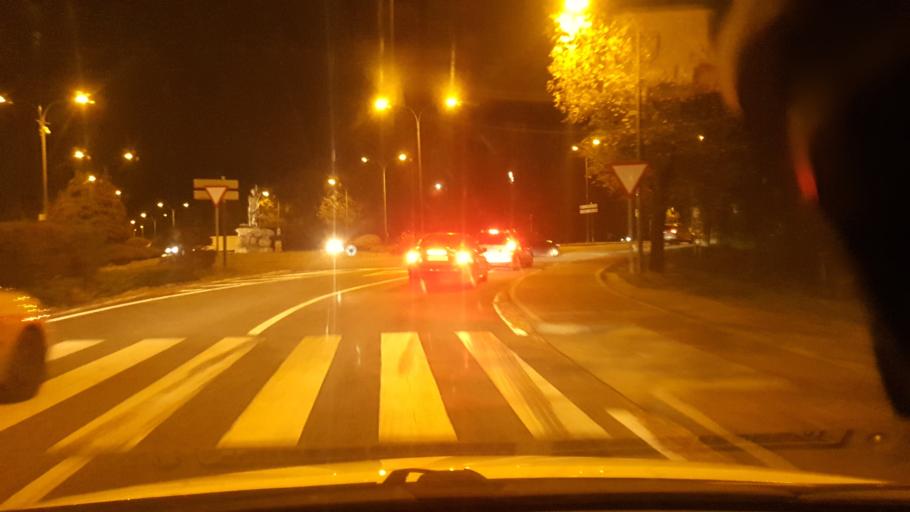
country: ES
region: Castille and Leon
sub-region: Provincia de Avila
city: Avila
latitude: 40.6487
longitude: -4.7045
